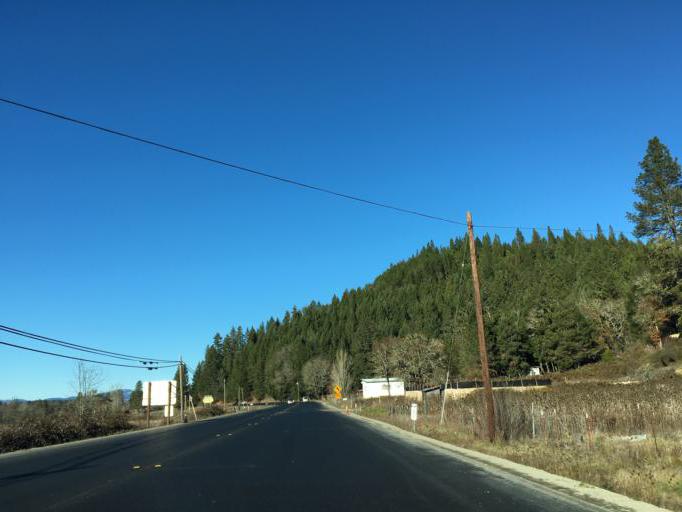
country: US
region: California
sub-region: Mendocino County
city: Laytonville
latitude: 39.6538
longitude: -123.4764
